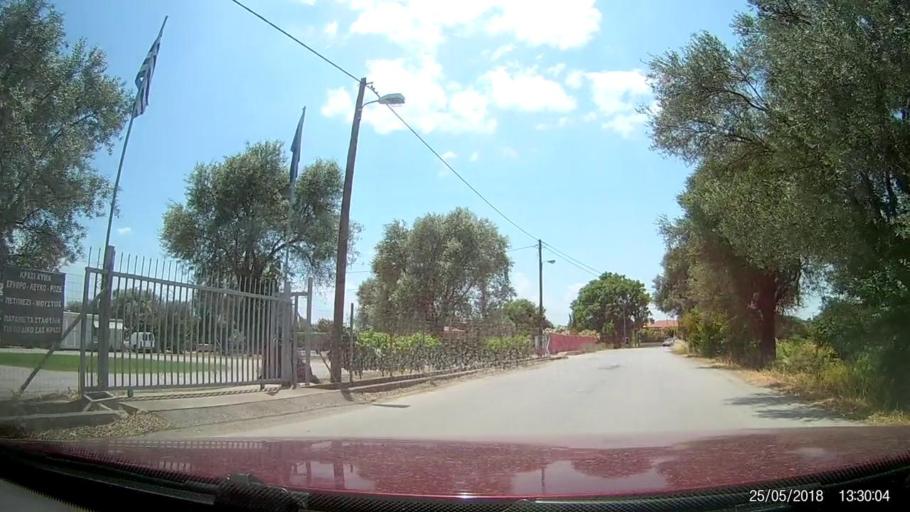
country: GR
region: Central Greece
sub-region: Nomos Evvoias
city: Mytikas
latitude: 38.4425
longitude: 23.6590
